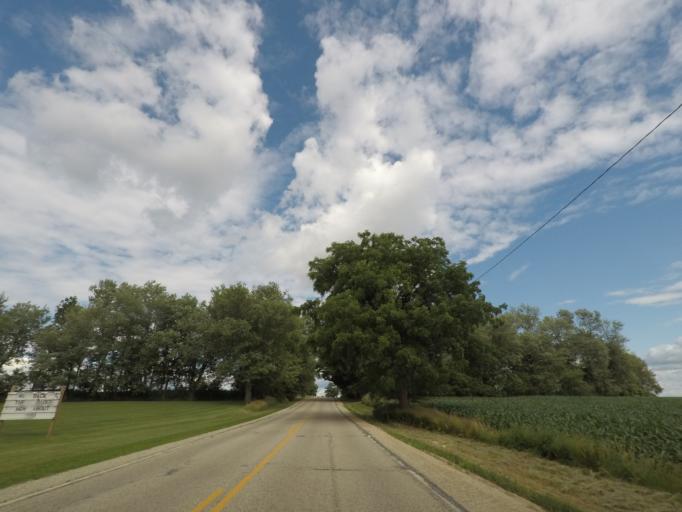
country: US
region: Wisconsin
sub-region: Rock County
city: Orfordville
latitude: 42.7122
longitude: -89.2087
